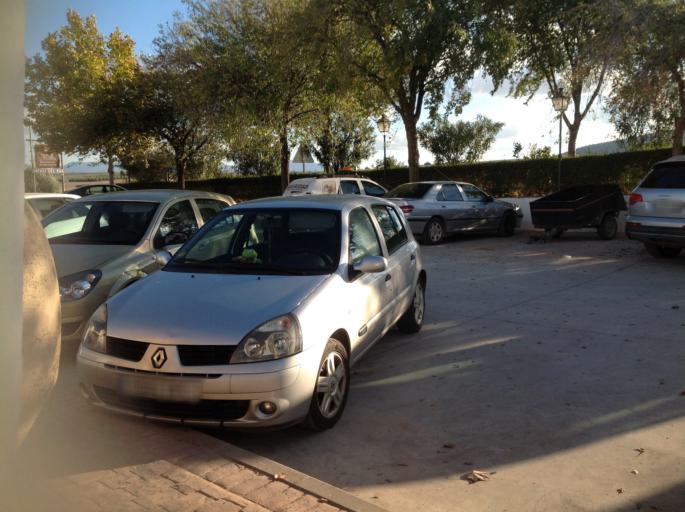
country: ES
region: Andalusia
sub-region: Provincia de Malaga
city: Alameda
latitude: 37.1995
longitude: -4.6416
